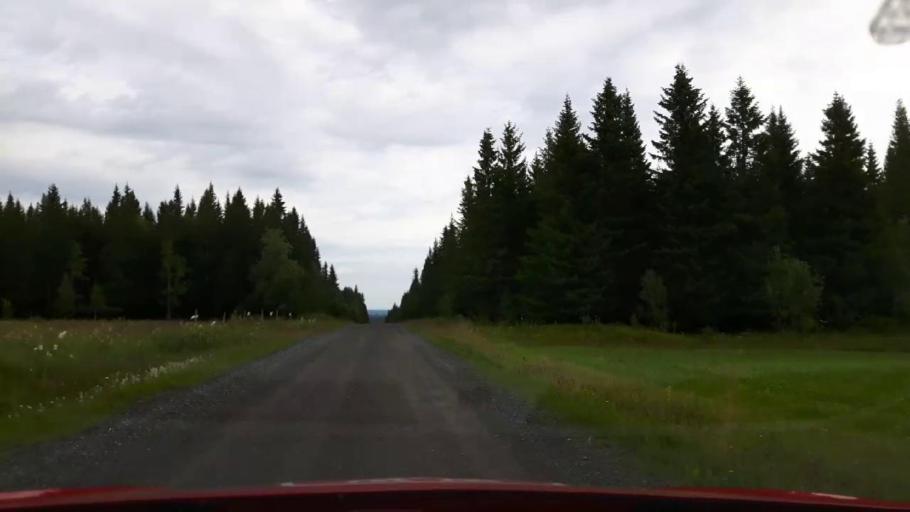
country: SE
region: Jaemtland
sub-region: OEstersunds Kommun
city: Lit
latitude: 63.3852
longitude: 15.2007
